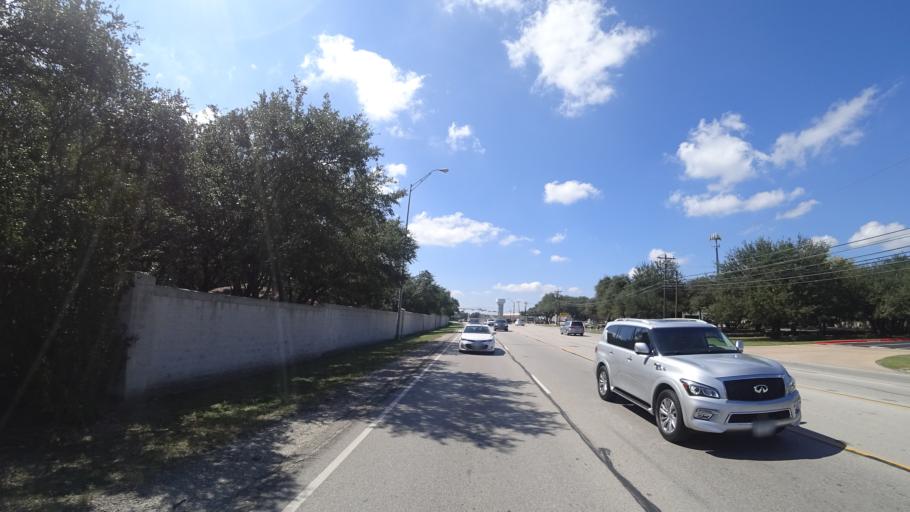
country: US
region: Texas
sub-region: Williamson County
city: Anderson Mill
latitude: 30.4613
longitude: -97.8185
